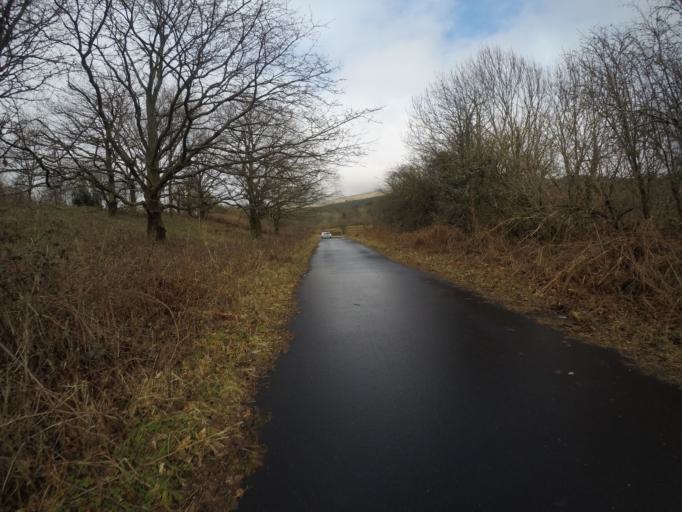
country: GB
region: Scotland
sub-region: North Ayrshire
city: Fairlie
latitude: 55.7335
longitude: -4.8631
